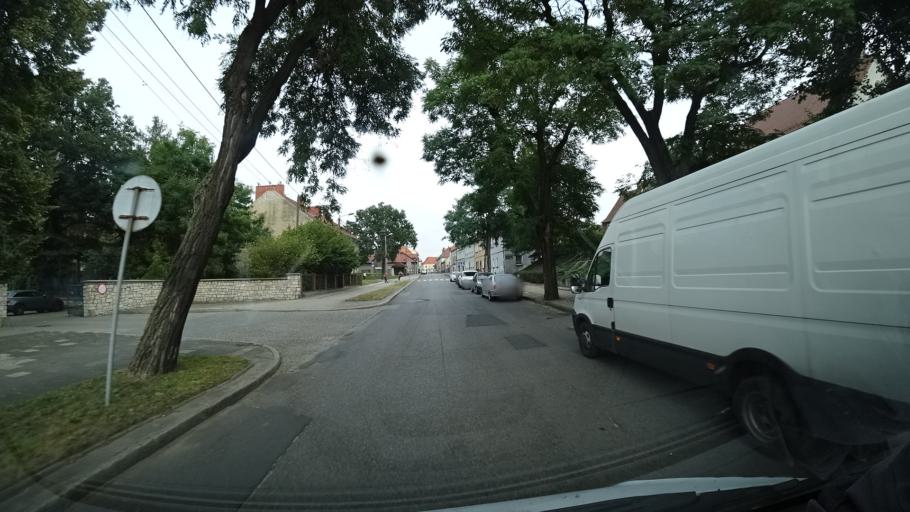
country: PL
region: Silesian Voivodeship
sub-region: Powiat gliwicki
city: Pyskowice
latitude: 50.3980
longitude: 18.6238
